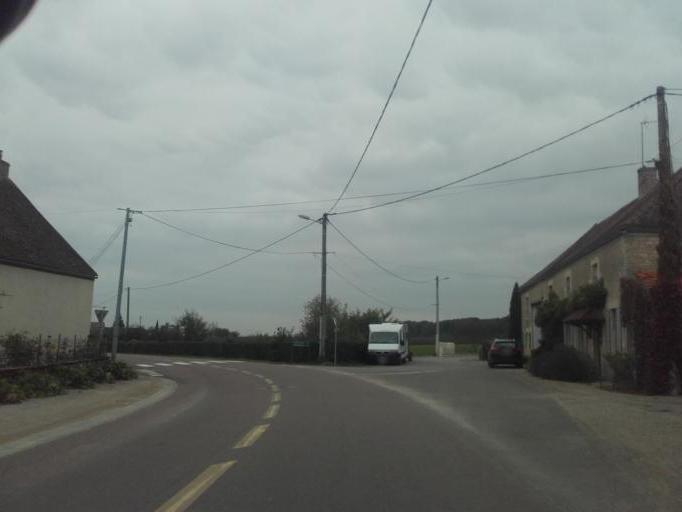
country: FR
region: Bourgogne
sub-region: Departement de Saone-et-Loire
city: Demigny
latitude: 46.9575
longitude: 4.8580
